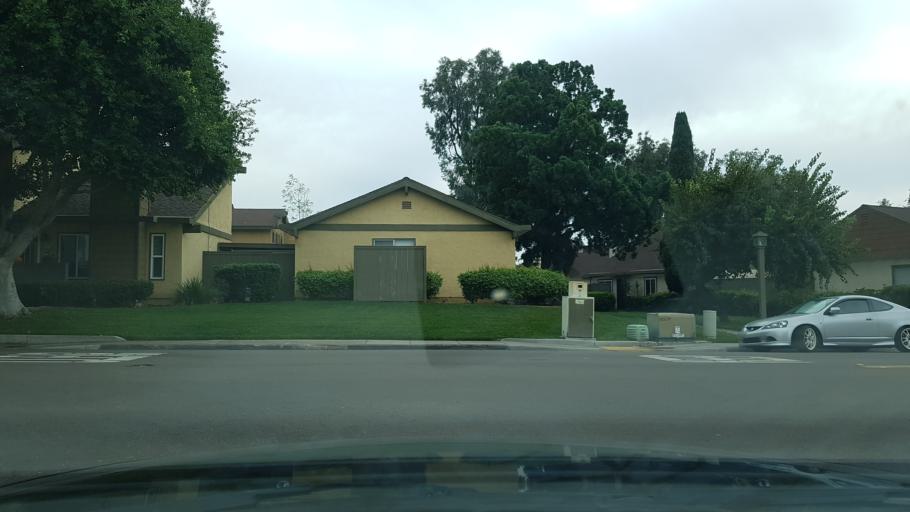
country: US
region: California
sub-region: San Diego County
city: Fairbanks Ranch
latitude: 32.9130
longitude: -117.1291
